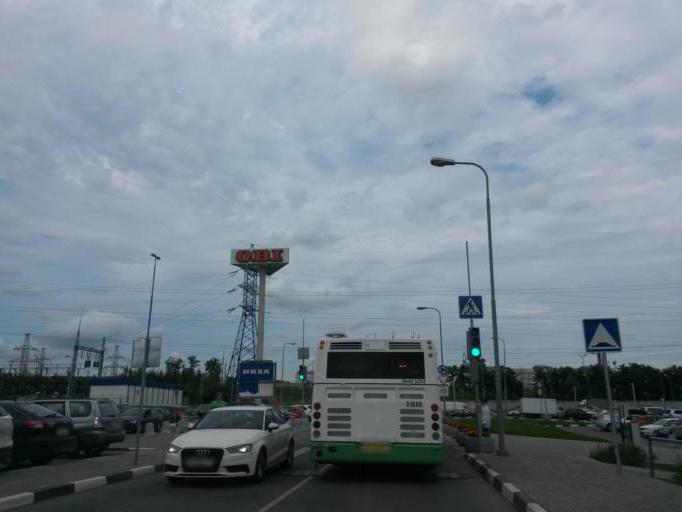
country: RU
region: Moscow
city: Tyoply Stan
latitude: 55.6029
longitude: 37.4979
